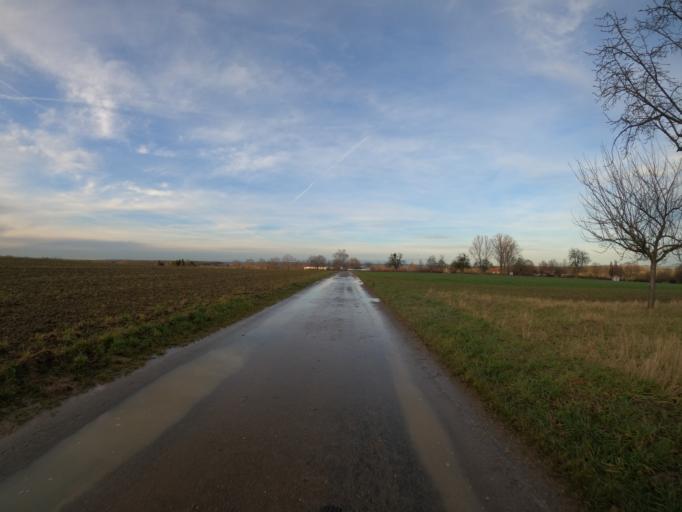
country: DE
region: Baden-Wuerttemberg
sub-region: Regierungsbezirk Stuttgart
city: Zell unter Aichelberg
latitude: 48.6414
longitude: 9.5823
